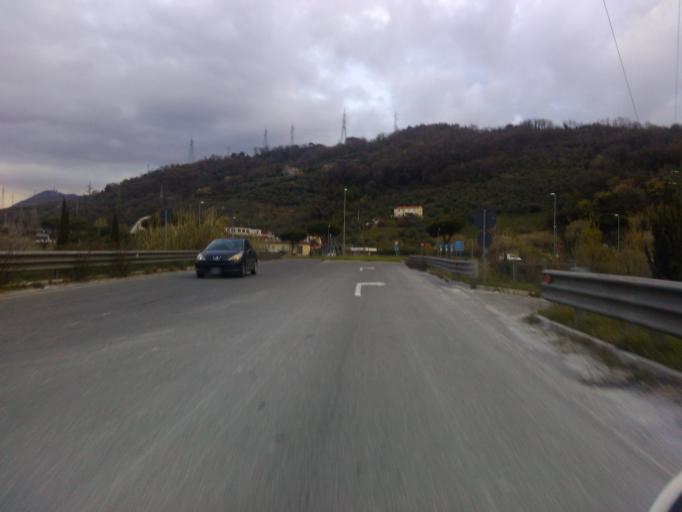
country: IT
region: Tuscany
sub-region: Provincia di Massa-Carrara
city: Carrara
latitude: 44.0424
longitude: 10.0858
